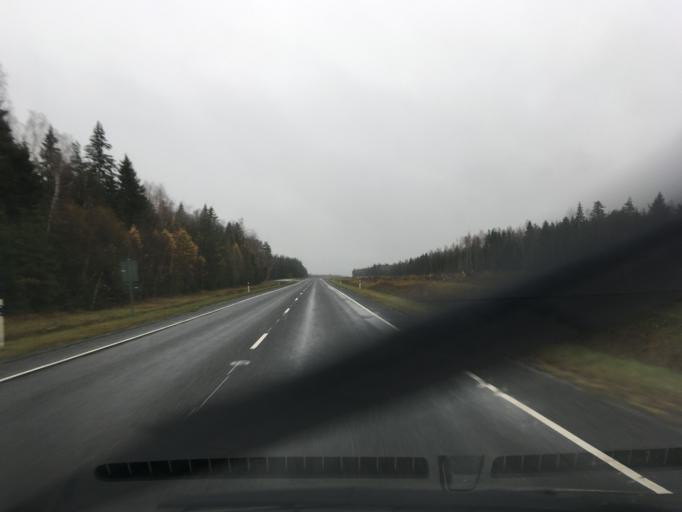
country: EE
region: Harju
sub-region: Nissi vald
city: Turba
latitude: 58.9630
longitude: 24.0717
